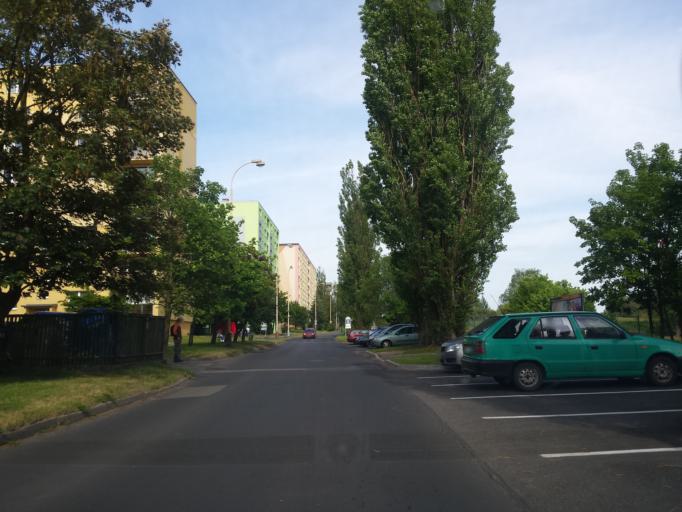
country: CZ
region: Liberecky
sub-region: Okres Ceska Lipa
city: Ceska Lipa
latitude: 50.6875
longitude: 14.5486
